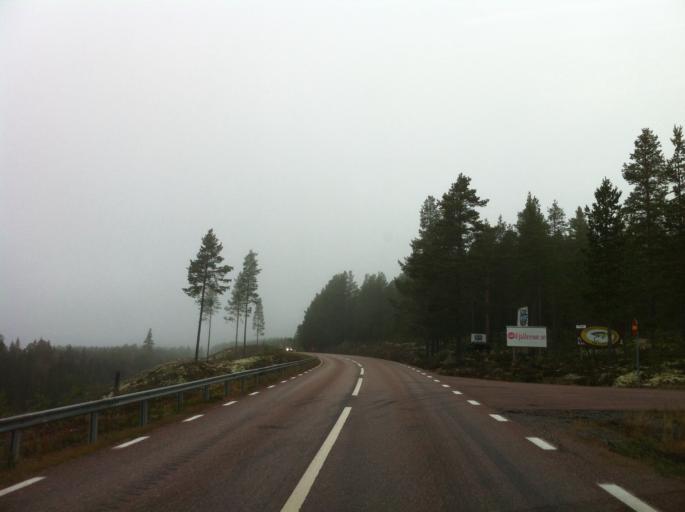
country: NO
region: Hedmark
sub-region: Trysil
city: Innbygda
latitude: 61.8474
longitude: 12.7695
